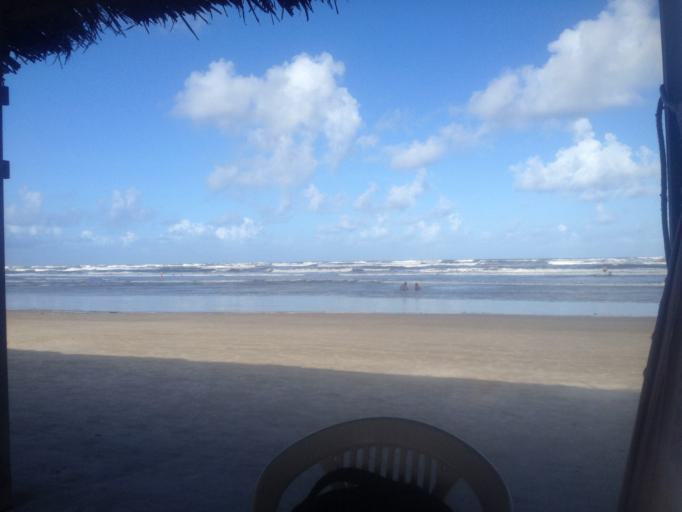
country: BR
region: Sergipe
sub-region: Indiaroba
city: Indiaroba
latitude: -11.4675
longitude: -37.3548
